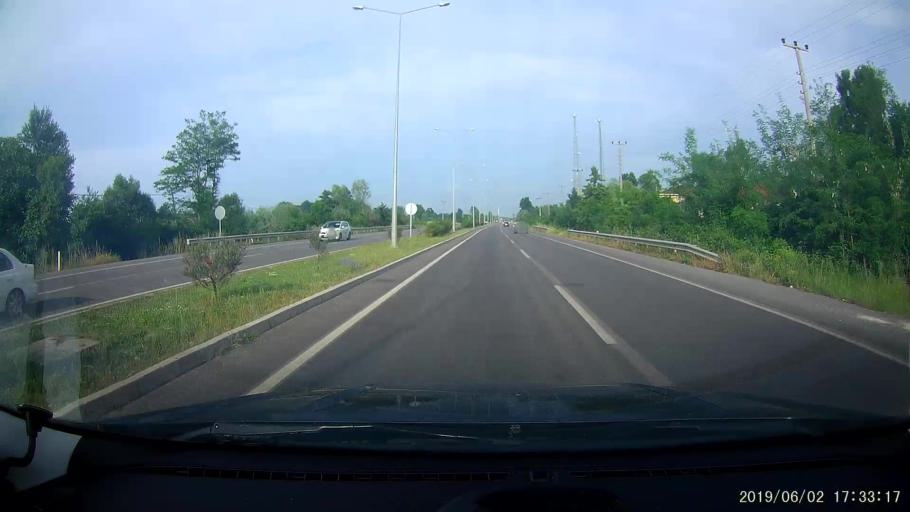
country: TR
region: Samsun
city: Carsamba
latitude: 41.2208
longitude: 36.8453
